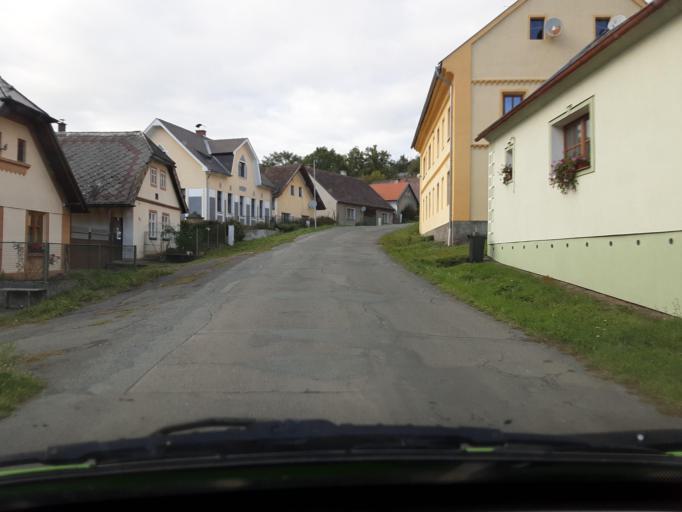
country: CZ
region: Plzensky
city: Janovice nad Uhlavou
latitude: 49.4256
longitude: 13.1761
